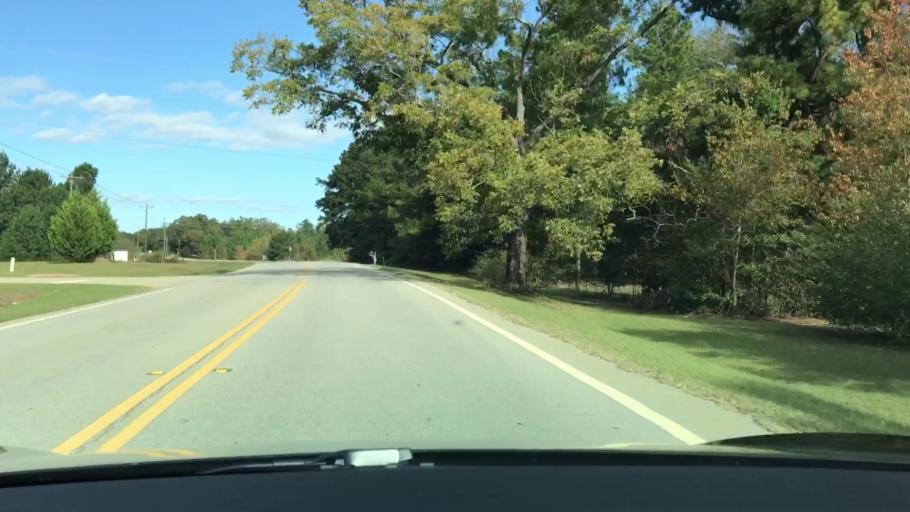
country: US
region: Georgia
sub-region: Jefferson County
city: Wrens
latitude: 33.1865
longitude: -82.4551
